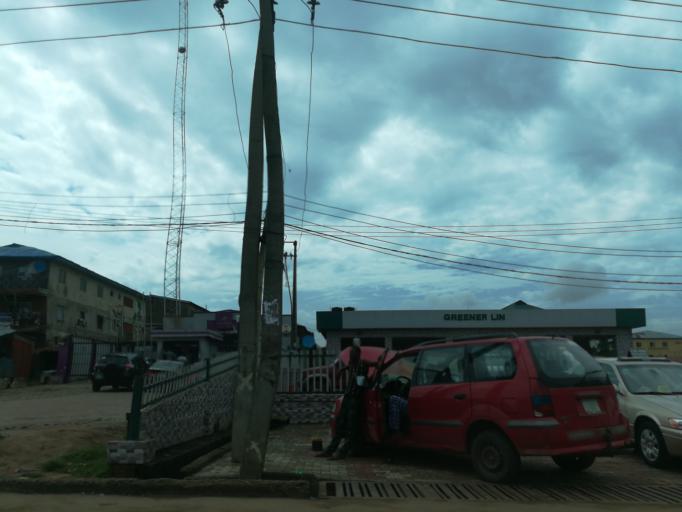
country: NG
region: Lagos
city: Ikorodu
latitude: 6.6230
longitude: 3.5045
